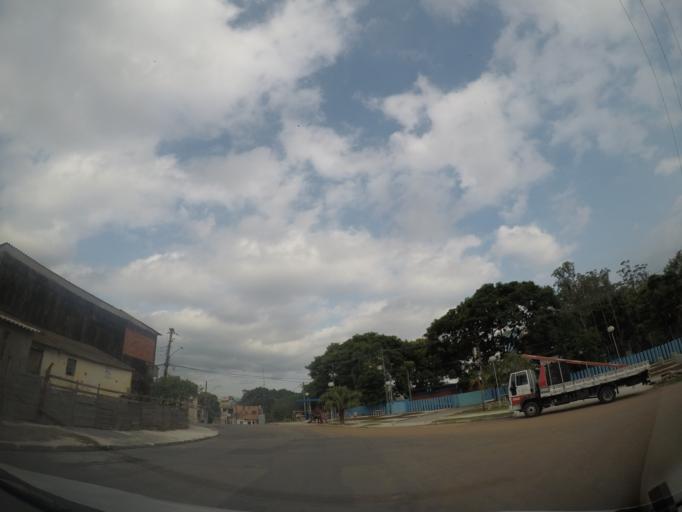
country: BR
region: Sao Paulo
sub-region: Guarulhos
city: Guarulhos
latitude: -23.4156
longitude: -46.5109
